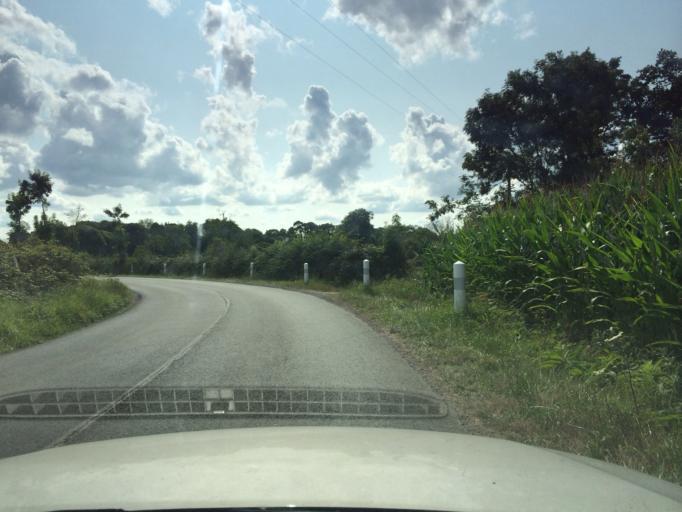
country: FR
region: Lower Normandy
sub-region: Departement du Calvados
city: Saint-Vigor-le-Grand
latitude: 49.3323
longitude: -0.6385
